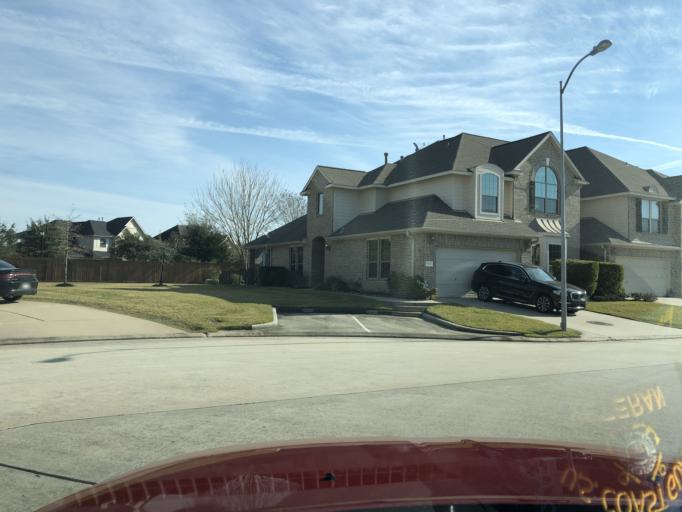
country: US
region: Texas
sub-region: Harris County
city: Tomball
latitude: 30.0396
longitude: -95.5535
